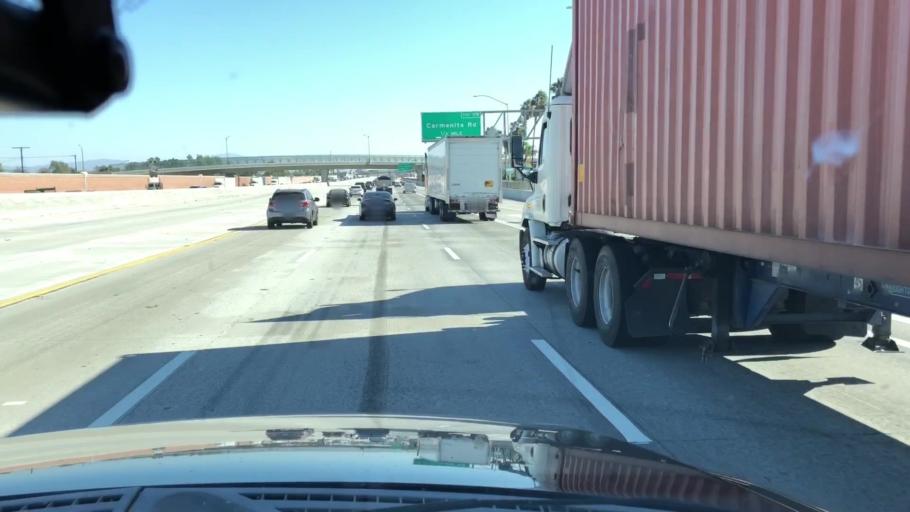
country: US
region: California
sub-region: Los Angeles County
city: Norwalk
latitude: 33.9001
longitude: -118.0588
